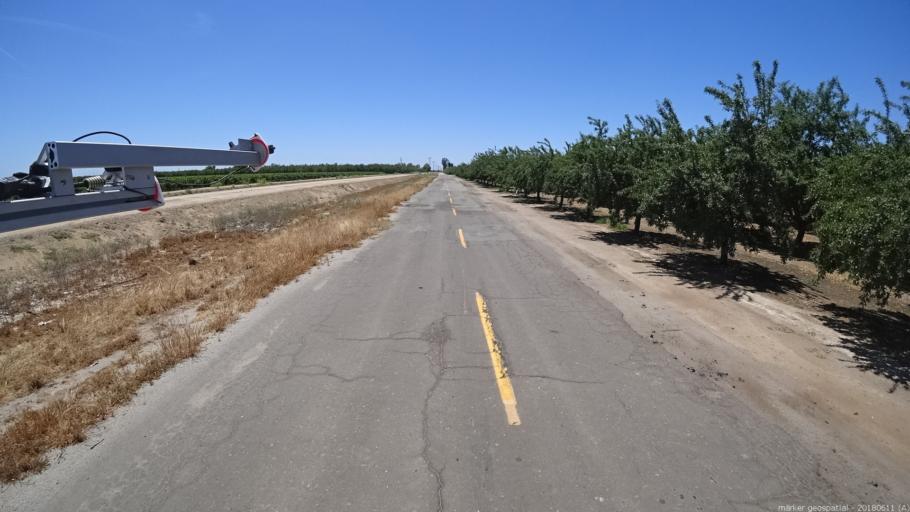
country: US
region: California
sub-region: Madera County
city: Fairmead
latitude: 37.0205
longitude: -120.2206
